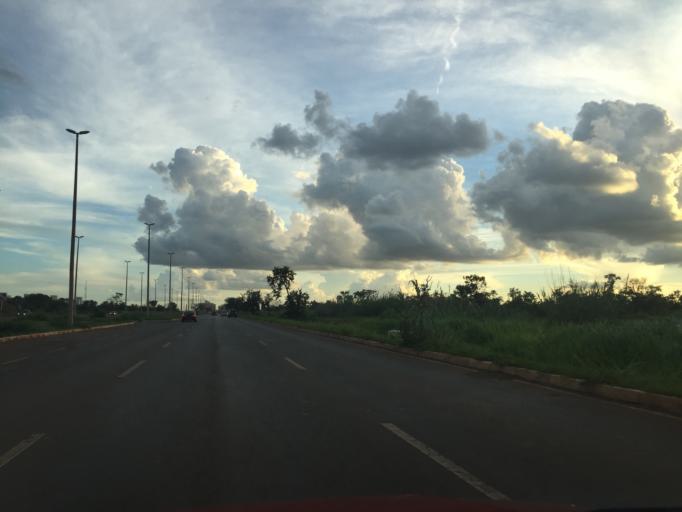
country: BR
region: Federal District
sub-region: Brasilia
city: Brasilia
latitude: -15.8025
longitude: -47.9918
